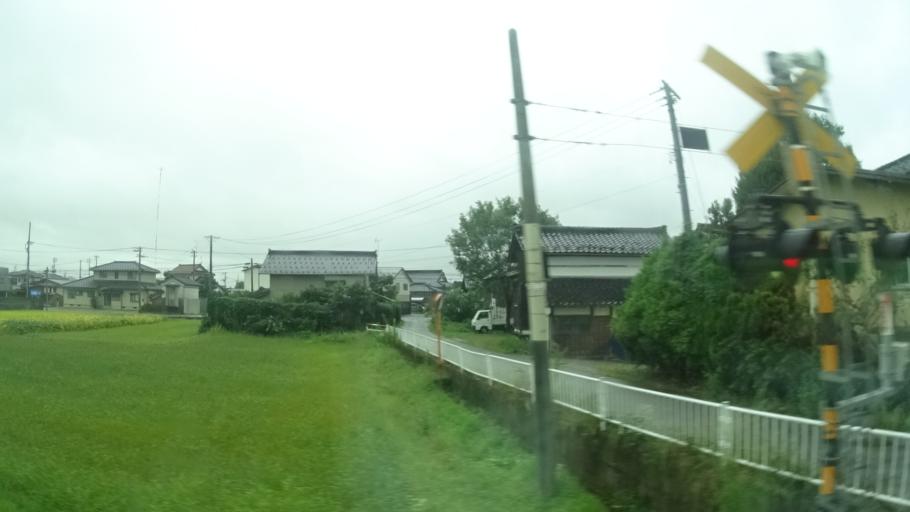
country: JP
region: Yamagata
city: Tsuruoka
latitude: 38.7393
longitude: 139.8560
